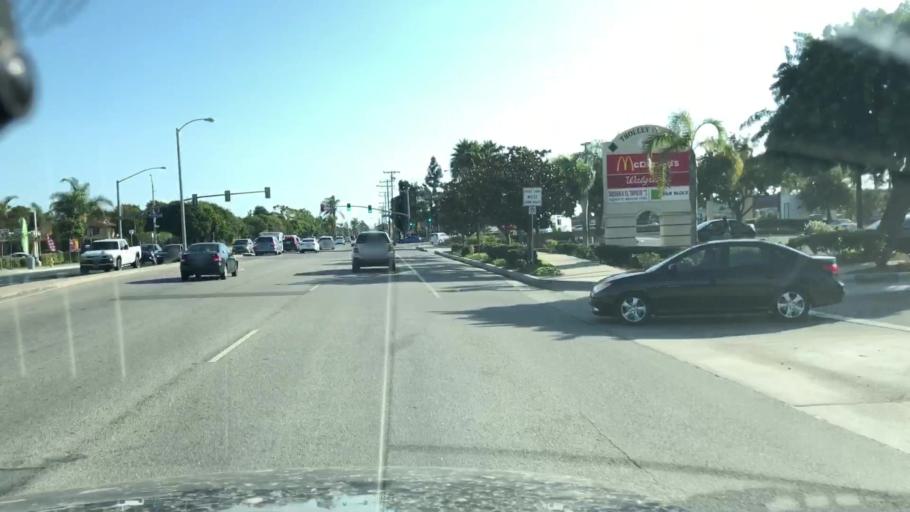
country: US
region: California
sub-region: Ventura County
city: Oxnard
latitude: 34.1988
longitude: -119.1949
